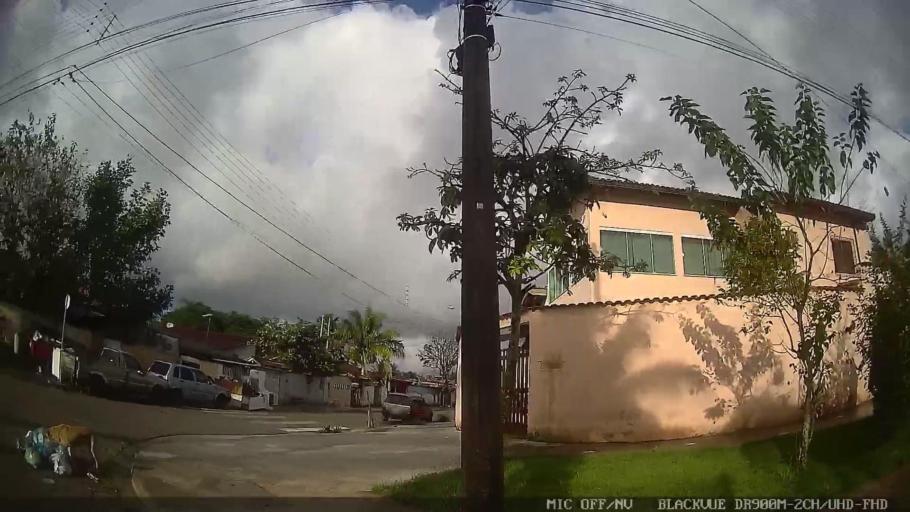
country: BR
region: Sao Paulo
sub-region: Itanhaem
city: Itanhaem
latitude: -24.2041
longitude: -46.8734
